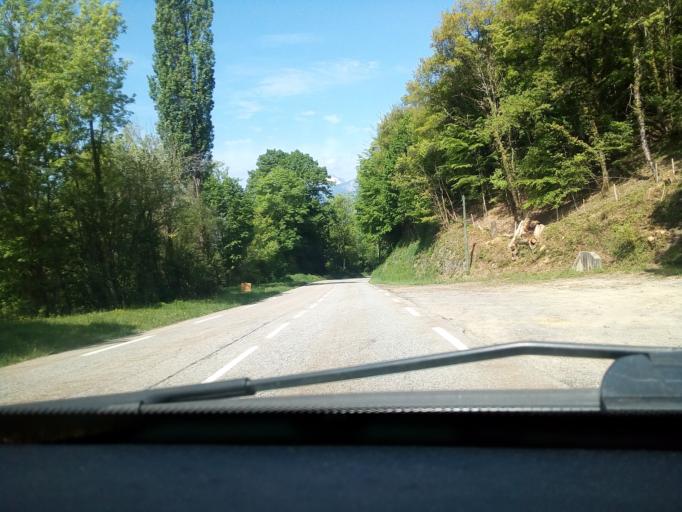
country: FR
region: Rhone-Alpes
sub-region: Departement de l'Isere
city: Le Champ-pres-Froges
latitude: 45.2699
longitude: 5.9535
